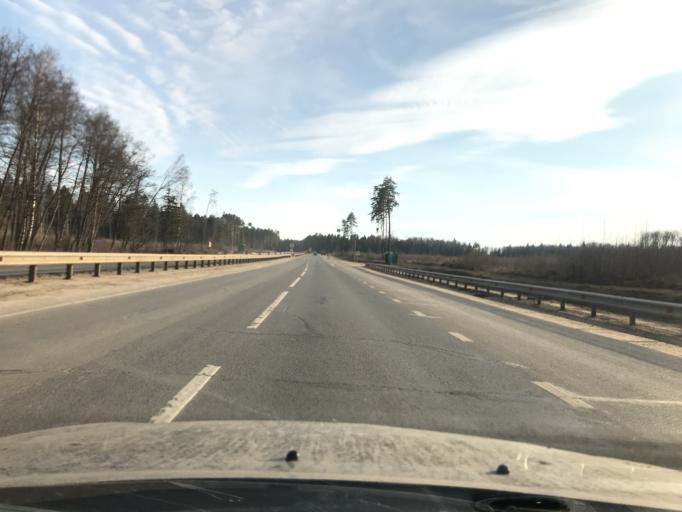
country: RU
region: Kaluga
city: Kaluga
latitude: 54.4207
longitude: 36.2032
